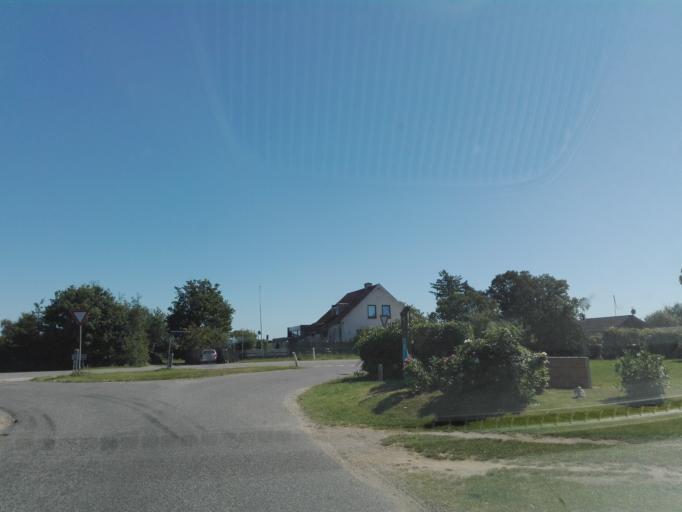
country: DK
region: Central Jutland
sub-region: Arhus Kommune
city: Malling
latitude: 55.9970
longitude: 10.2534
